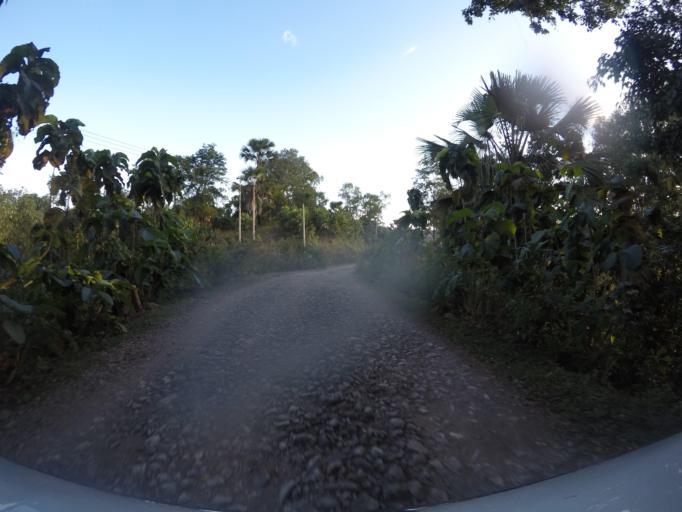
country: TL
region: Baucau
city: Venilale
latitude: -8.7199
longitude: 126.7121
